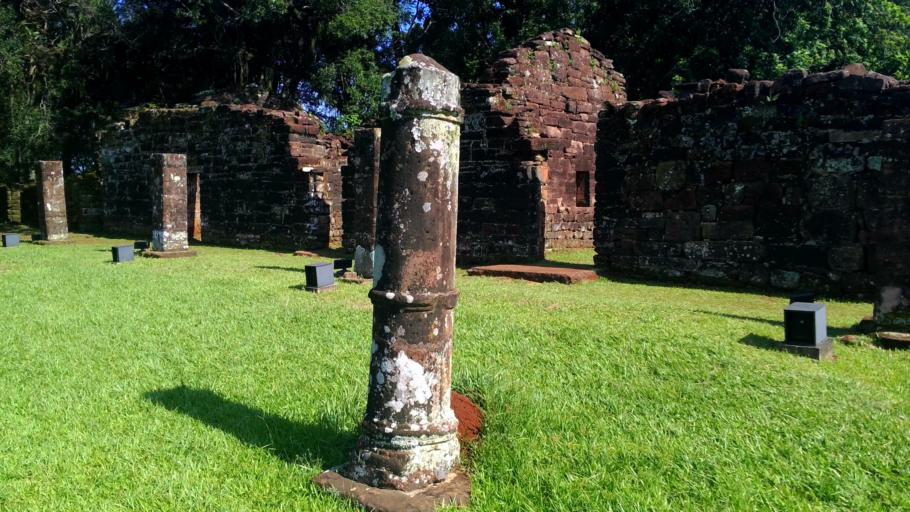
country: AR
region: Misiones
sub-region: Departamento de San Ignacio
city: San Ignacio
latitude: -27.2539
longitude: -55.5318
